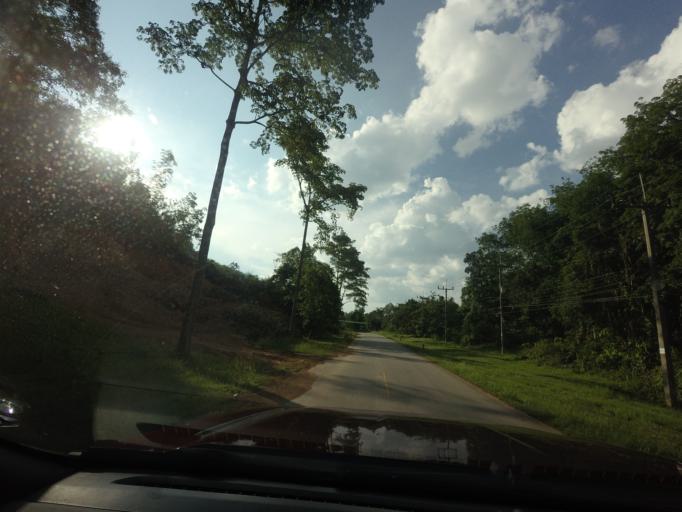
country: TH
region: Yala
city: Ban Nang Sata
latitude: 6.2099
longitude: 101.2343
